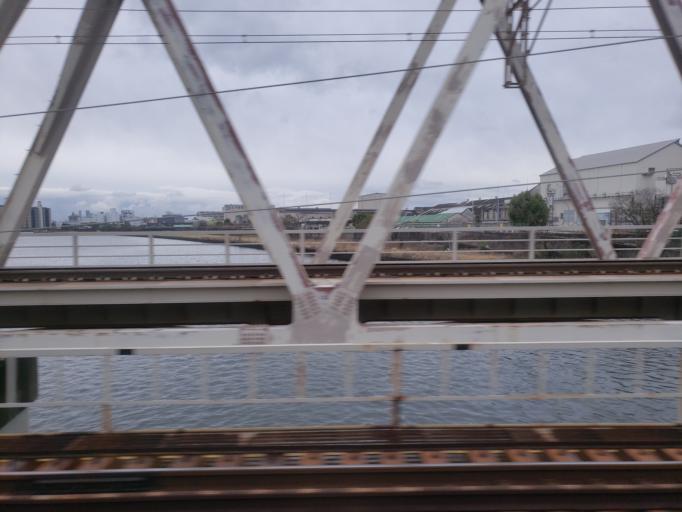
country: JP
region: Hyogo
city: Amagasaki
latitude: 34.7294
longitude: 135.4447
